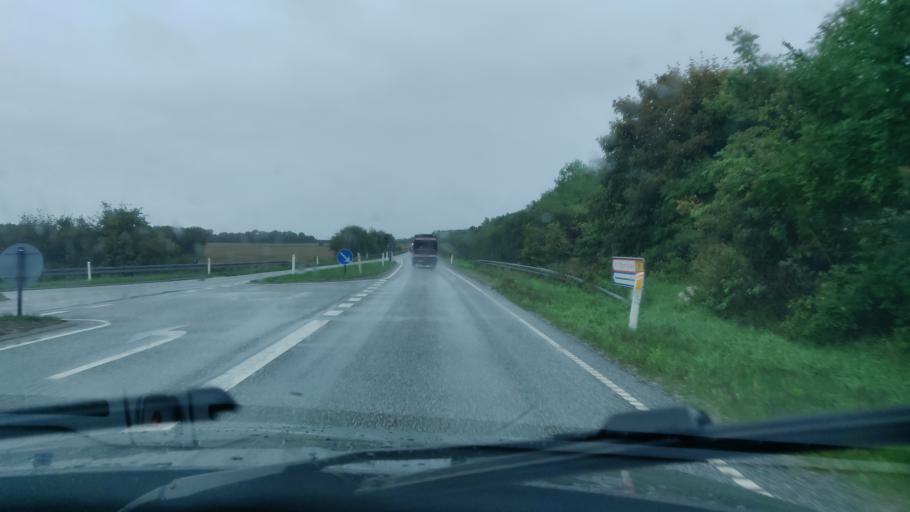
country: DK
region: North Denmark
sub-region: Thisted Kommune
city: Thisted
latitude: 56.9729
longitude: 8.6989
